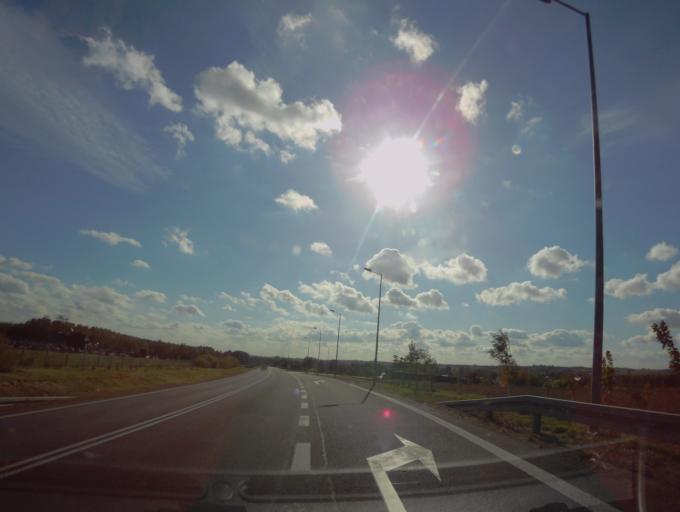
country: PL
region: Subcarpathian Voivodeship
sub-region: Powiat lezajski
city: Giedlarowa
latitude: 50.2426
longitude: 22.4098
